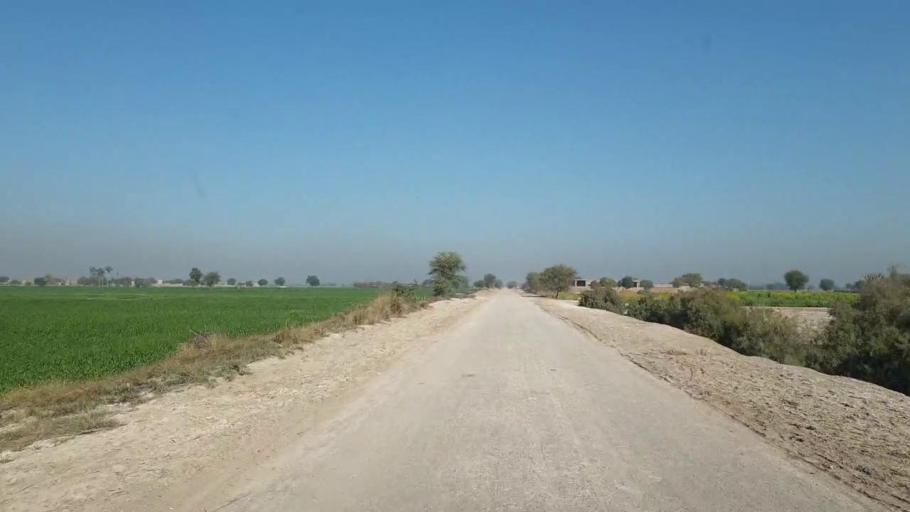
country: PK
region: Sindh
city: Shahdadpur
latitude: 25.9938
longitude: 68.4940
